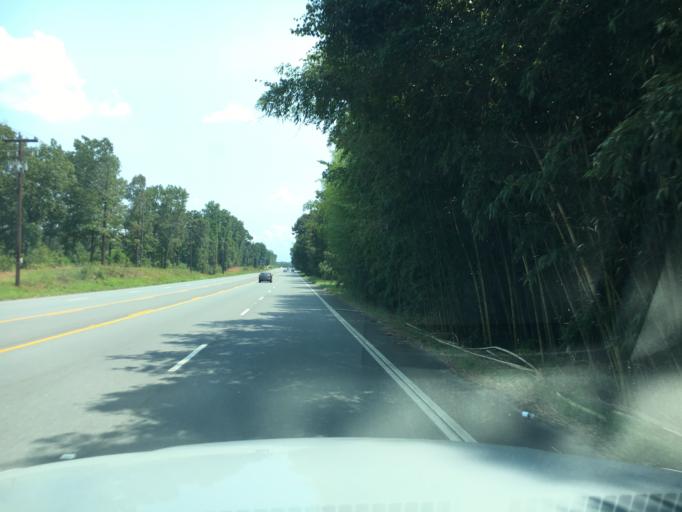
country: US
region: South Carolina
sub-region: Anderson County
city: Pendleton
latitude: 34.6204
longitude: -82.7761
